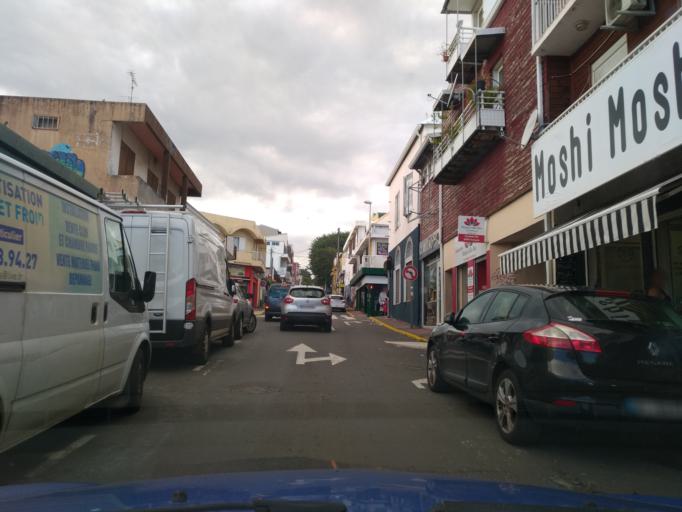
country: RE
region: Reunion
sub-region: Reunion
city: Saint-Pierre
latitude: -21.3385
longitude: 55.4760
